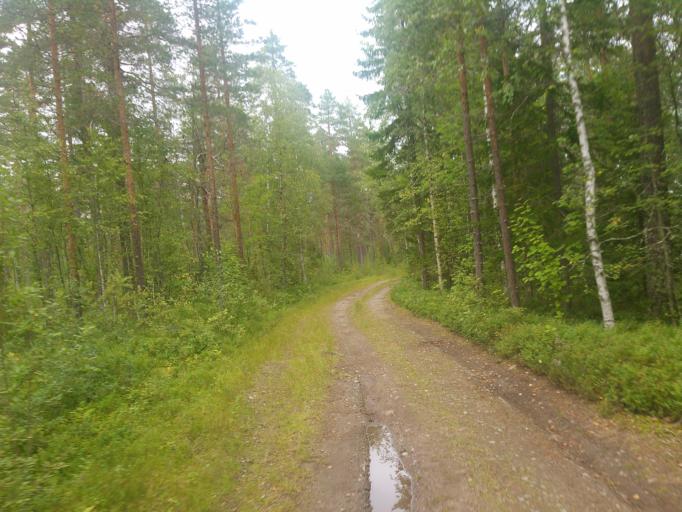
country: SE
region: Vaesterbotten
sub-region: Umea Kommun
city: Ersmark
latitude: 63.9294
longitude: 20.3823
